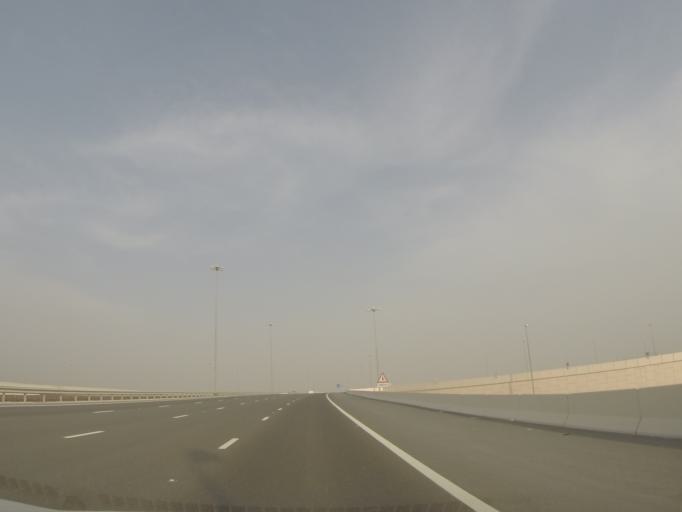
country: AE
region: Abu Dhabi
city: Abu Dhabi
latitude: 24.6958
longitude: 54.7765
